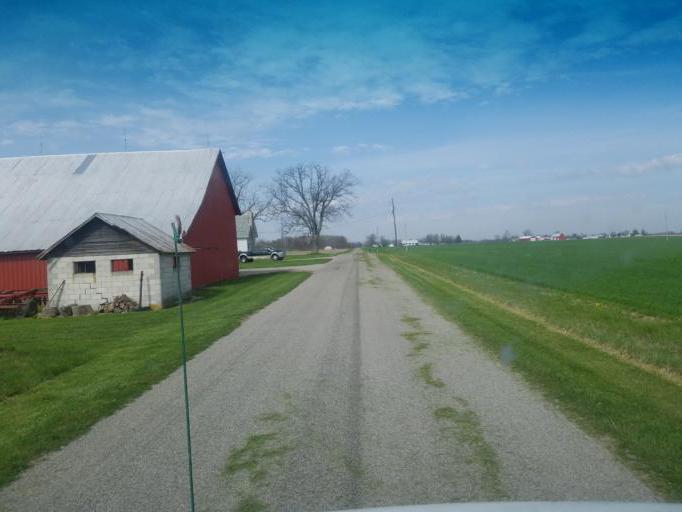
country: US
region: Ohio
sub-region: Union County
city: Richwood
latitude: 40.4824
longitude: -83.4687
